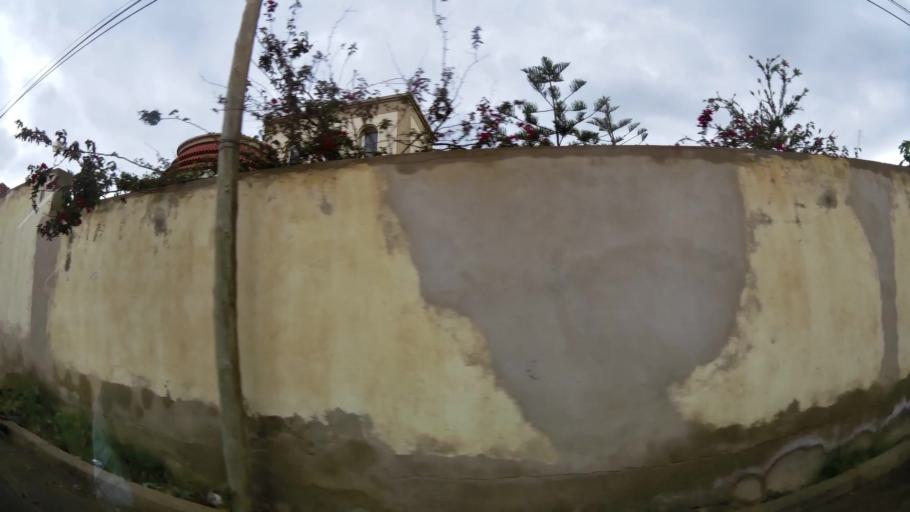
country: MA
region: Oriental
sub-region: Nador
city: Nador
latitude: 35.1492
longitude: -2.9888
